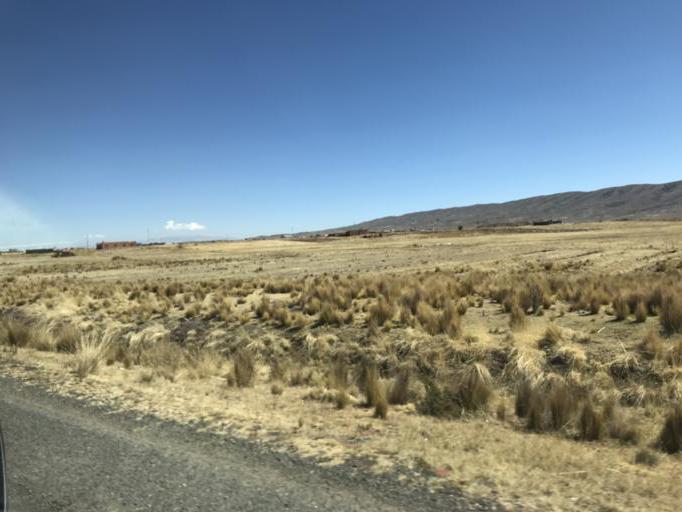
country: BO
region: La Paz
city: Tiahuanaco
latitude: -16.5695
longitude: -68.6641
